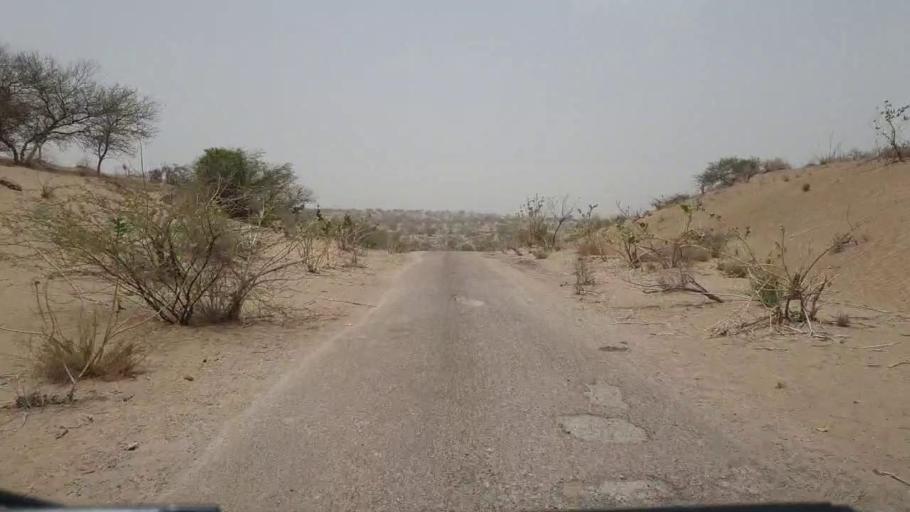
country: PK
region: Sindh
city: Naukot
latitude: 24.7396
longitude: 69.5477
